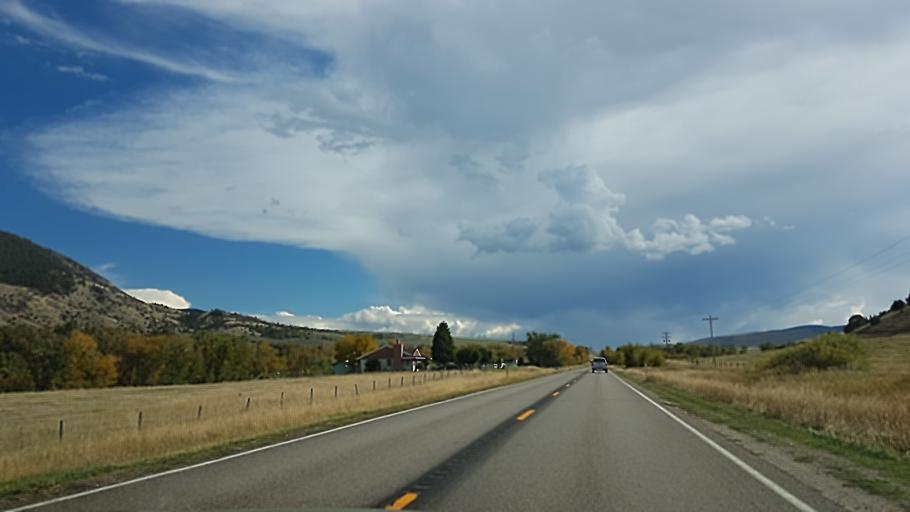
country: US
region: Montana
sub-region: Jefferson County
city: Whitehall
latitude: 45.8122
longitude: -111.9330
